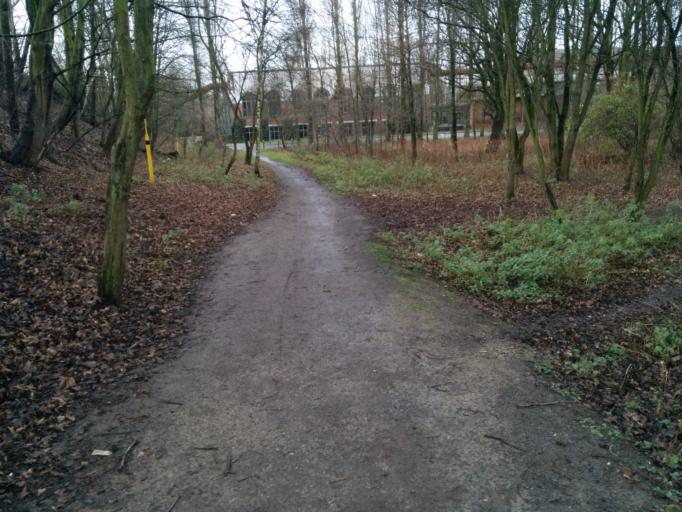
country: DE
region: North Rhine-Westphalia
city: Meiderich
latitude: 51.4775
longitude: 6.7790
